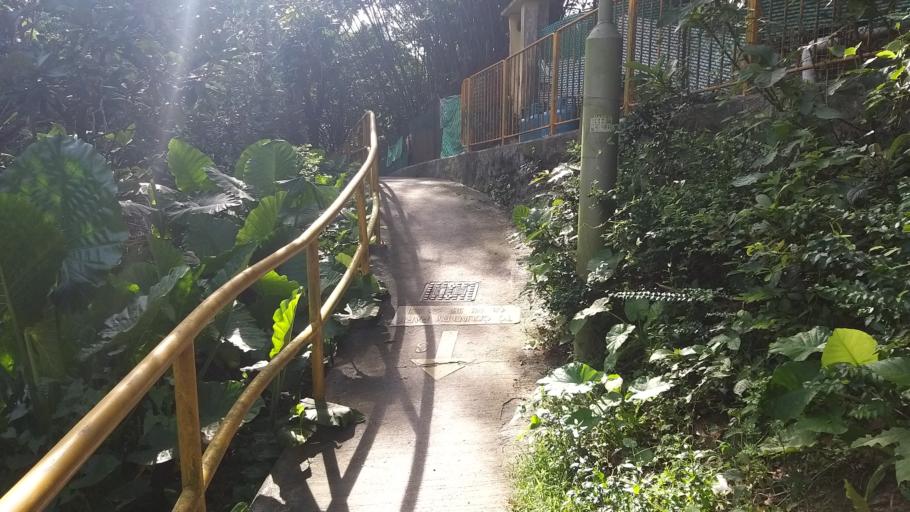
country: HK
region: Tuen Mun
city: Tuen Mun
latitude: 22.3950
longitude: 113.9799
